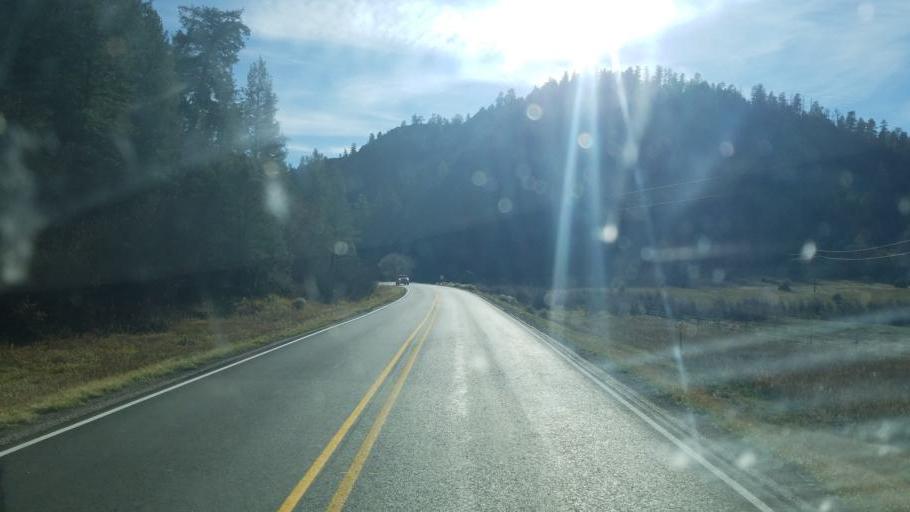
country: US
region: New Mexico
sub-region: Rio Arriba County
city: Dulce
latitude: 36.9047
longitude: -107.0032
